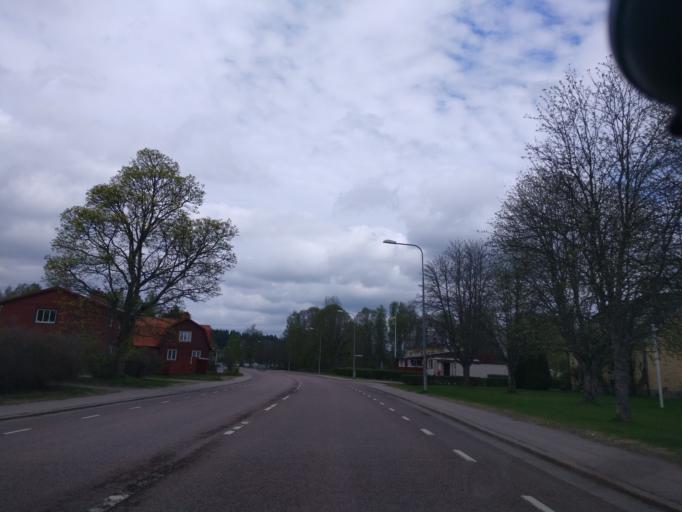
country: SE
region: Vaermland
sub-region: Hagfors Kommun
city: Ekshaerad
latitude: 60.1787
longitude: 13.4962
